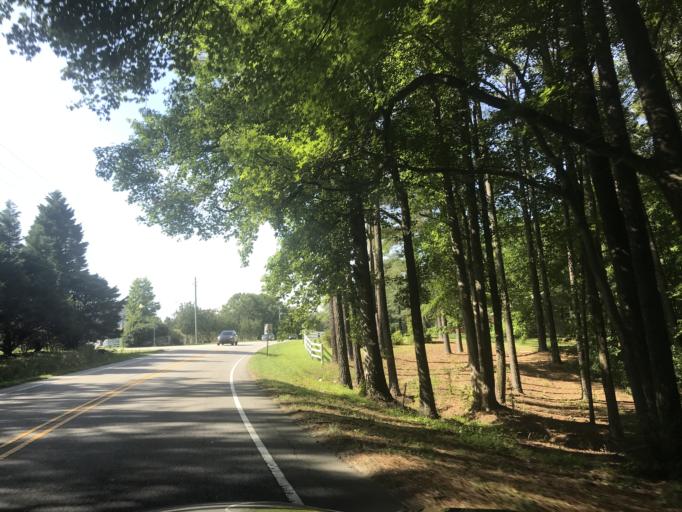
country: US
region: North Carolina
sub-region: Johnston County
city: Clayton
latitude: 35.6219
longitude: -78.5369
